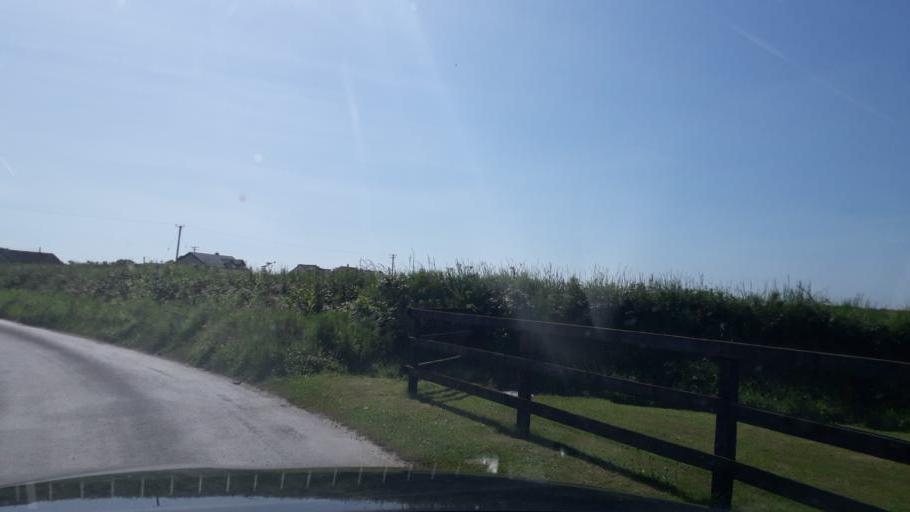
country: IE
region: Leinster
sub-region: Loch Garman
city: Loch Garman
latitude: 52.1877
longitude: -6.5417
